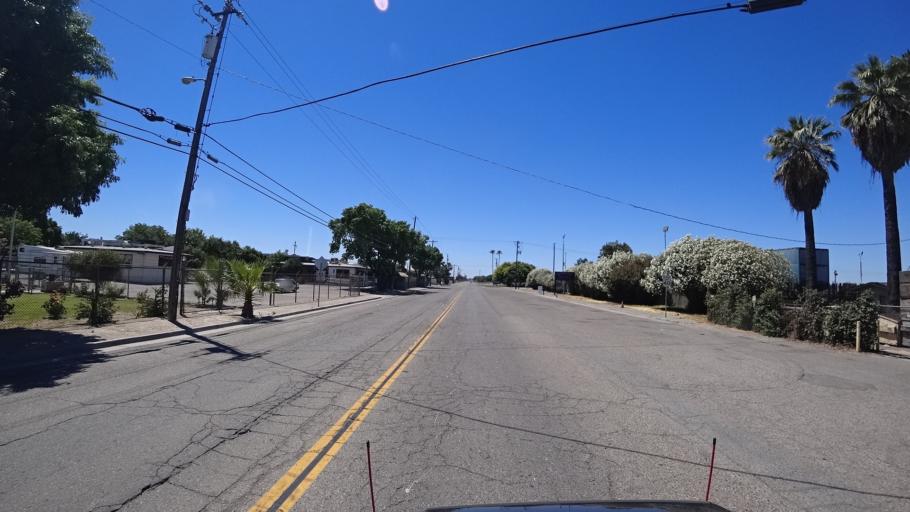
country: US
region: California
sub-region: Fresno County
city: Fresno
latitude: 36.7006
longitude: -119.7638
